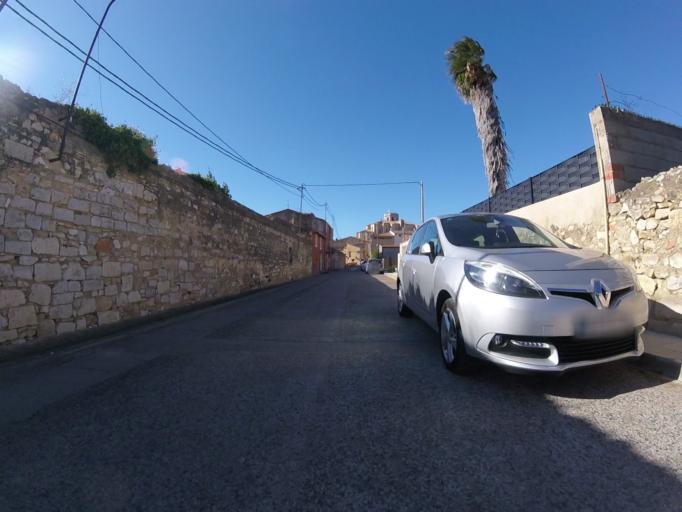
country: ES
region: Valencia
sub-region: Provincia de Castello
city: Chert/Xert
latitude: 40.4666
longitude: 0.1826
